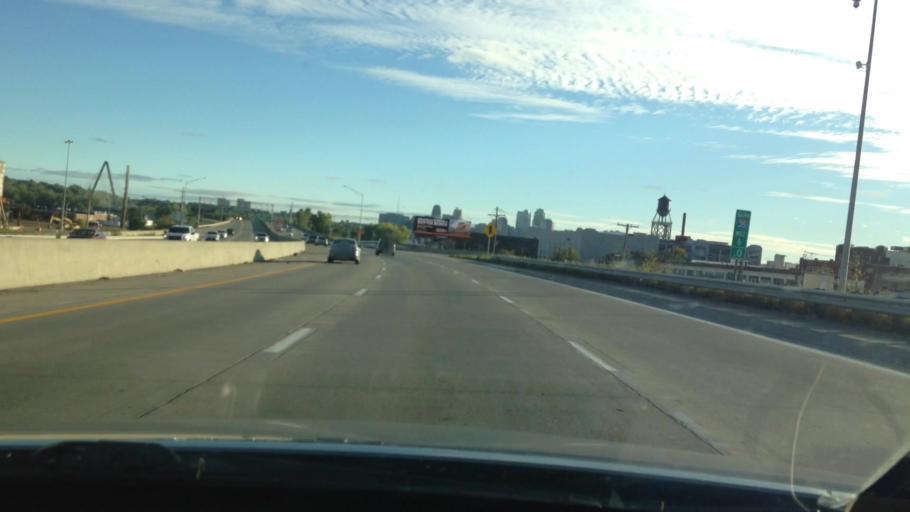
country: US
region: Missouri
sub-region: Clay County
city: North Kansas City
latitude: 39.1374
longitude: -94.5677
